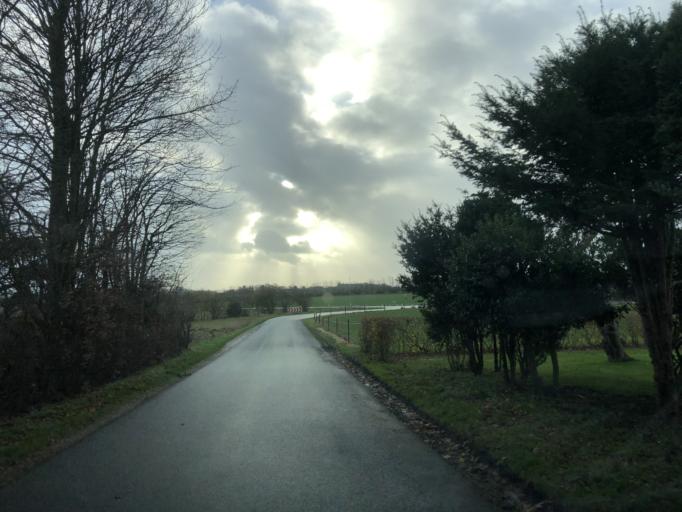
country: DK
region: North Denmark
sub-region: Rebild Kommune
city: Stovring
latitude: 56.8965
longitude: 9.7811
